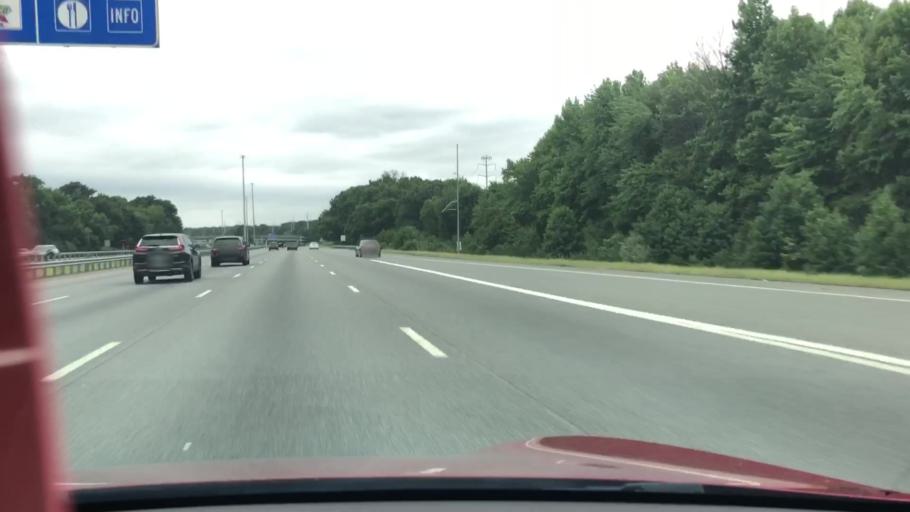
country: US
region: Delaware
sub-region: New Castle County
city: Bear
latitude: 39.6692
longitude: -75.6790
